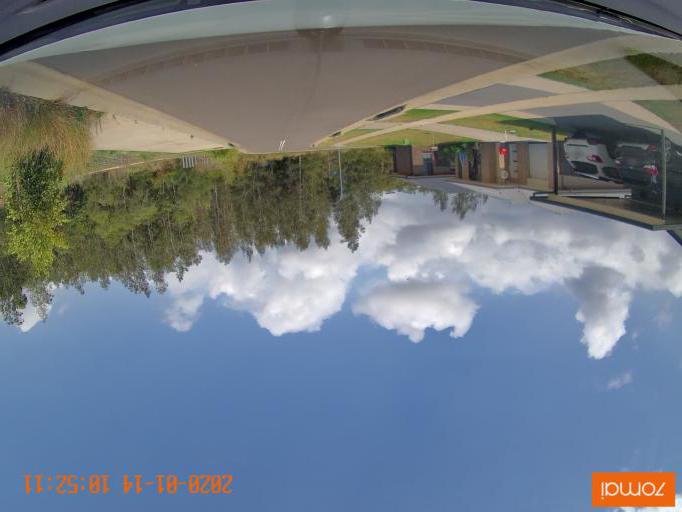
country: AU
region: New South Wales
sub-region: Lake Macquarie Shire
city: Dora Creek
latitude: -33.0997
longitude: 151.4827
